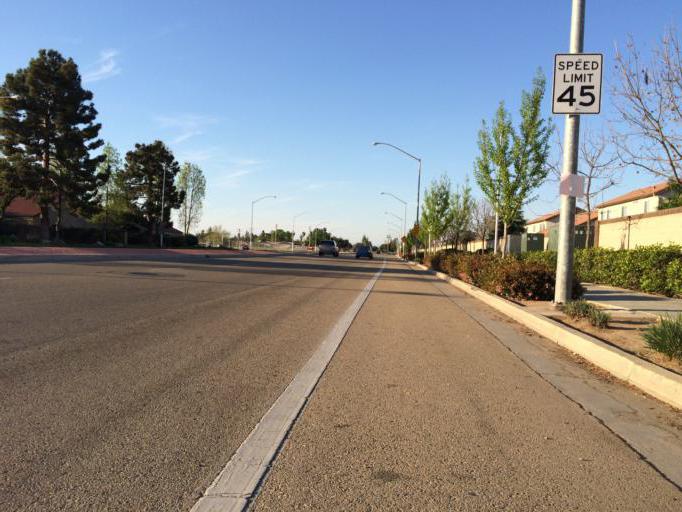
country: US
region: California
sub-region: Fresno County
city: Tarpey Village
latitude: 36.7798
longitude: -119.6821
